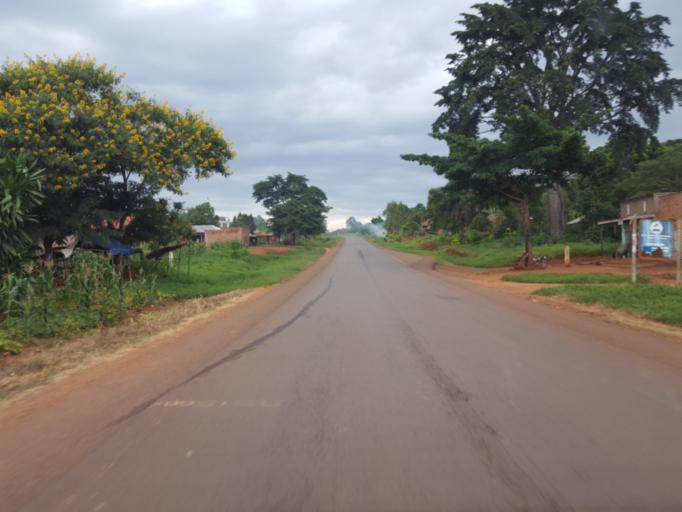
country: UG
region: Central Region
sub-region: Kiboga District
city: Kiboga
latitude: 0.8679
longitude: 31.8568
